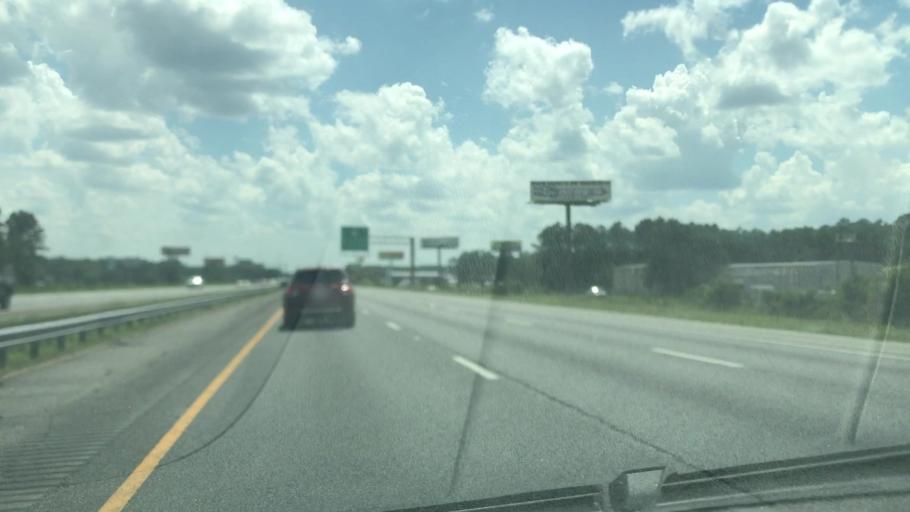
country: US
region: Georgia
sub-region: Bryan County
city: Richmond Hill
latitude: 31.9684
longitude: -81.3211
